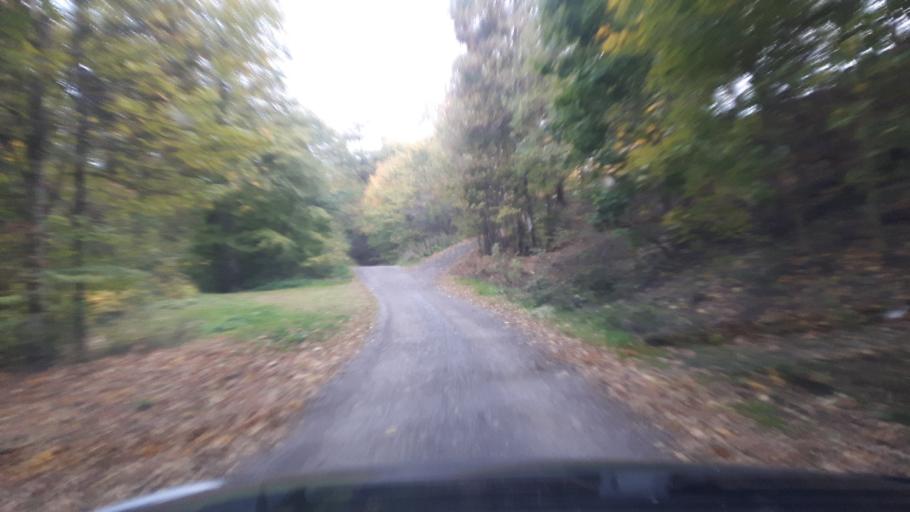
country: DE
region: North Rhine-Westphalia
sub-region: Regierungsbezirk Arnsberg
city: Bad Laasphe
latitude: 50.9321
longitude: 8.3966
